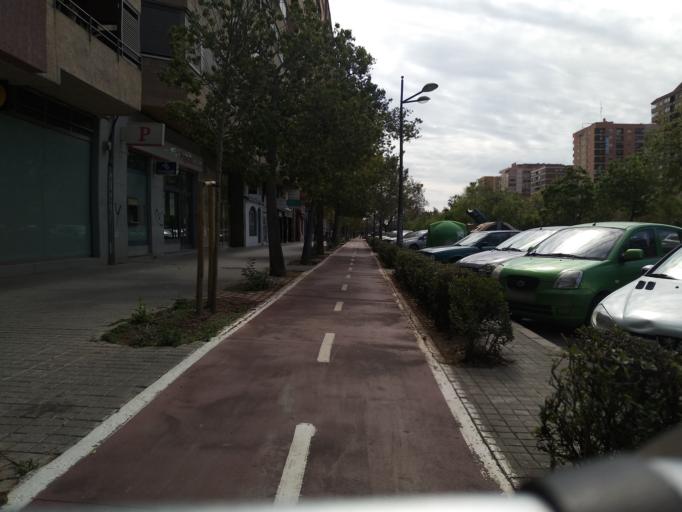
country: ES
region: Valencia
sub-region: Provincia de Valencia
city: Alboraya
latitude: 39.4741
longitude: -0.3469
